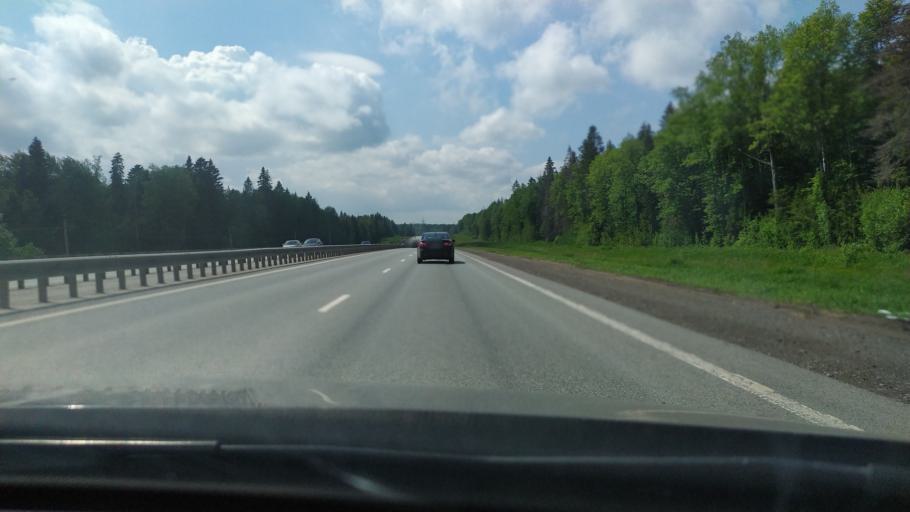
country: RU
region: Perm
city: Ferma
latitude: 58.0240
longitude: 56.4232
